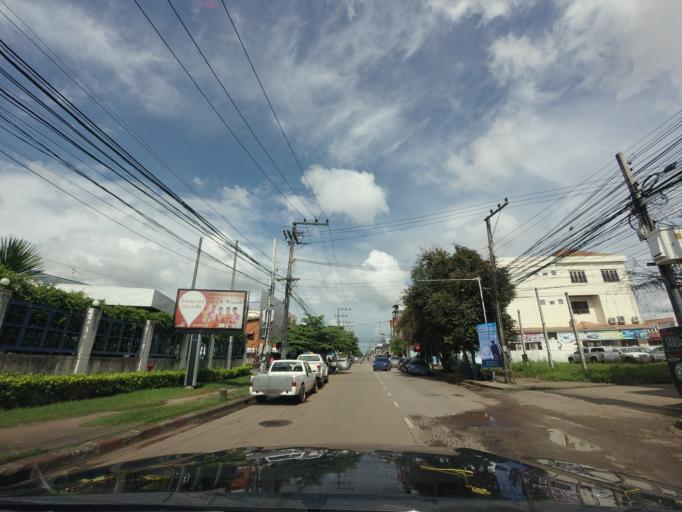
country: TH
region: Changwat Udon Thani
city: Udon Thani
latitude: 17.4071
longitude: 102.8034
